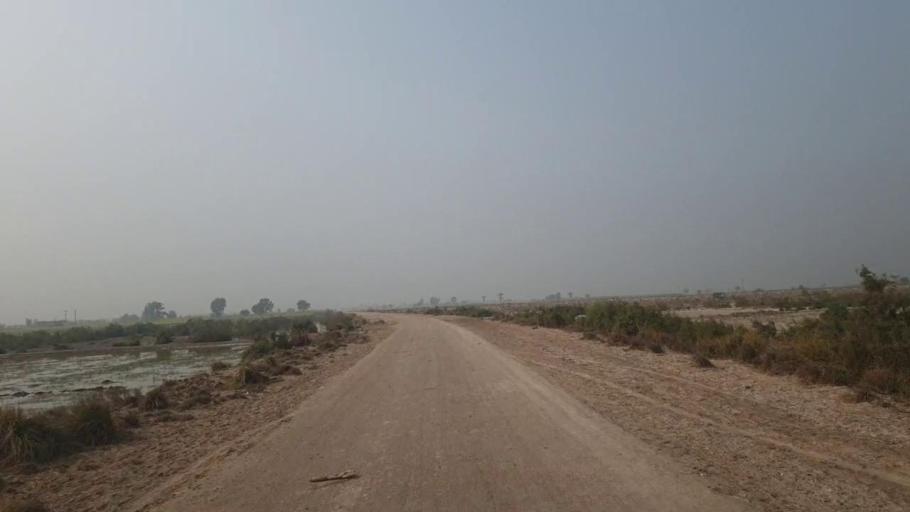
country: PK
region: Sindh
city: Shahdadpur
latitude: 25.8353
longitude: 68.5899
